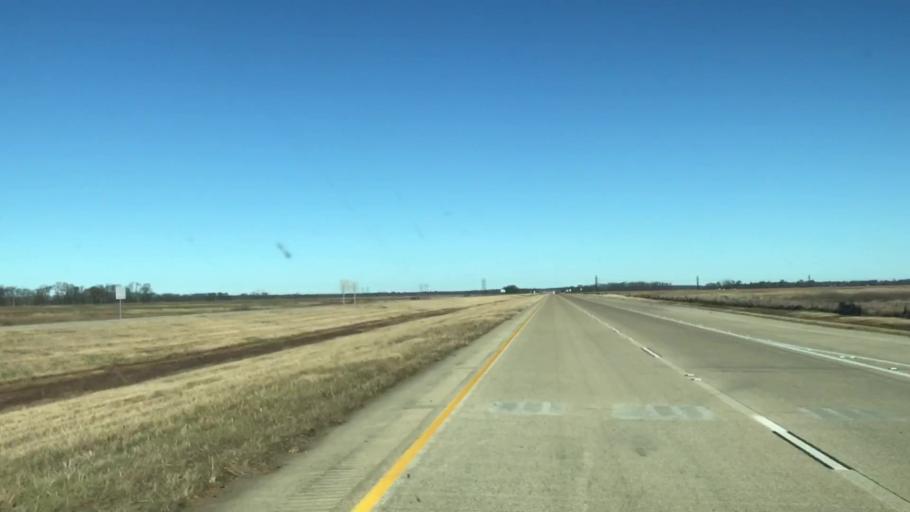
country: US
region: Louisiana
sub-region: Caddo Parish
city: Oil City
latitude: 32.7067
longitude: -93.8632
